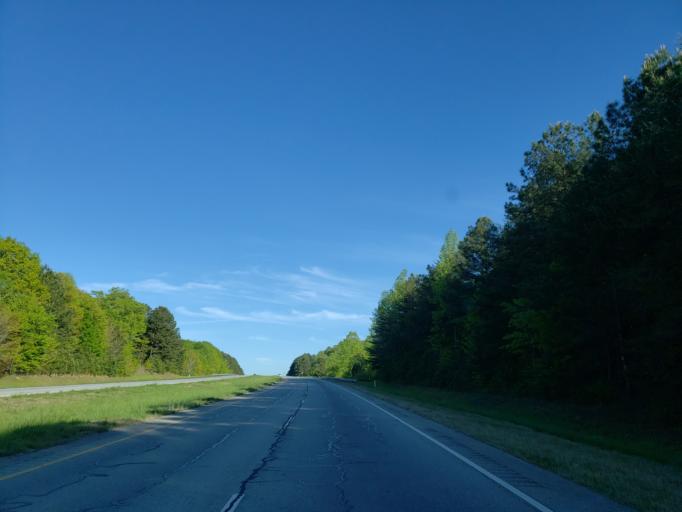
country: US
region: Georgia
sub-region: Polk County
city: Rockmart
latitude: 33.9376
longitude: -84.9729
